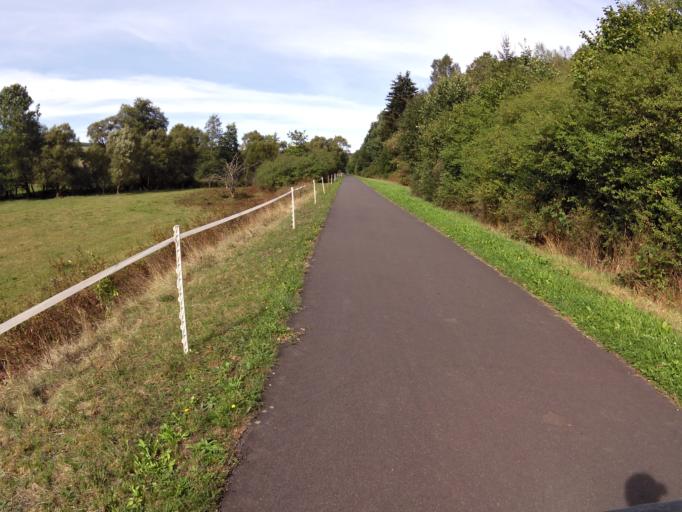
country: DE
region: Rheinland-Pfalz
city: Pronsfeld
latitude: 50.1665
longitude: 6.3175
